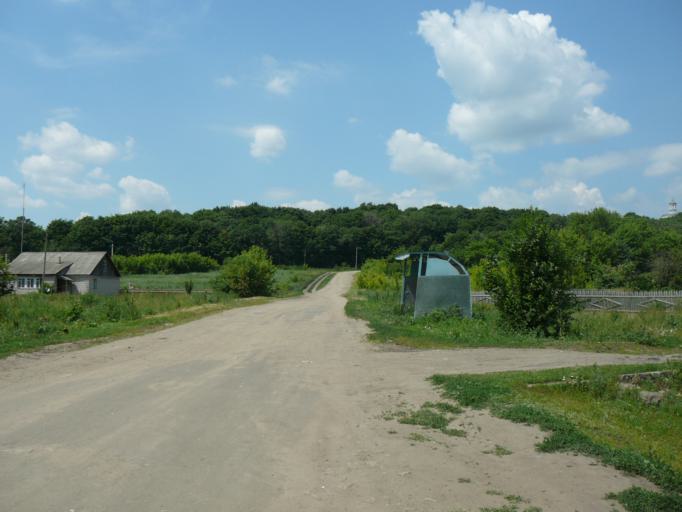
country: RU
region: Penza
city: Tamala
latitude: 52.3896
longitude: 43.3866
